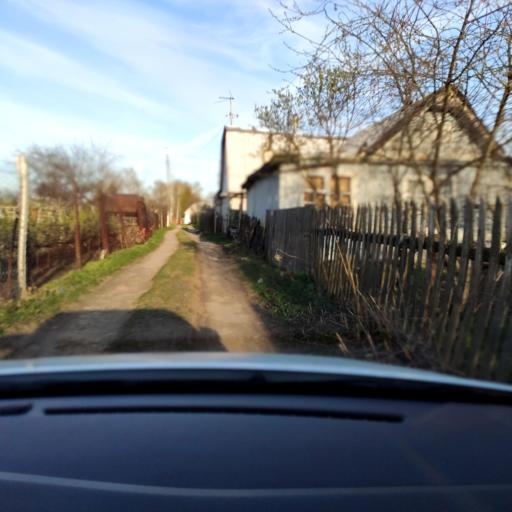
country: RU
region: Tatarstan
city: Stolbishchi
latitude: 55.6012
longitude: 49.0979
